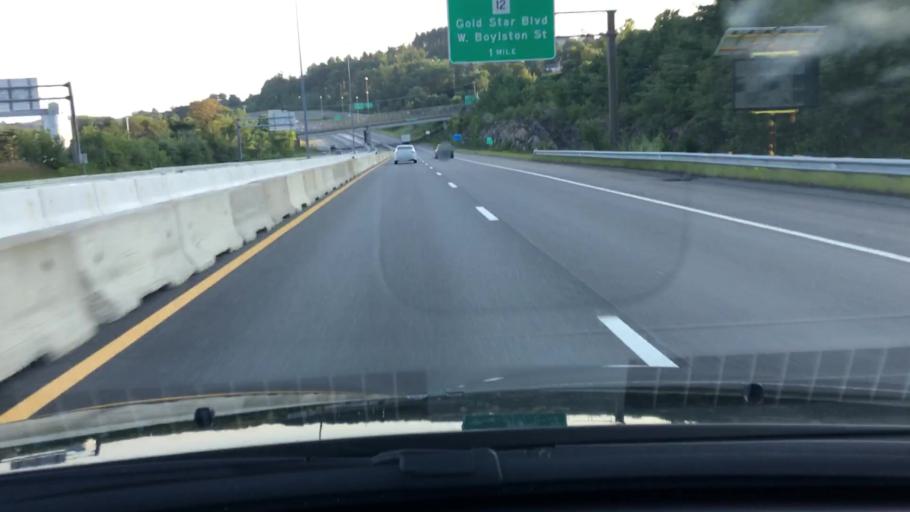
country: US
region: Massachusetts
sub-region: Worcester County
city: West Boylston
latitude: 42.3170
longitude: -71.8051
